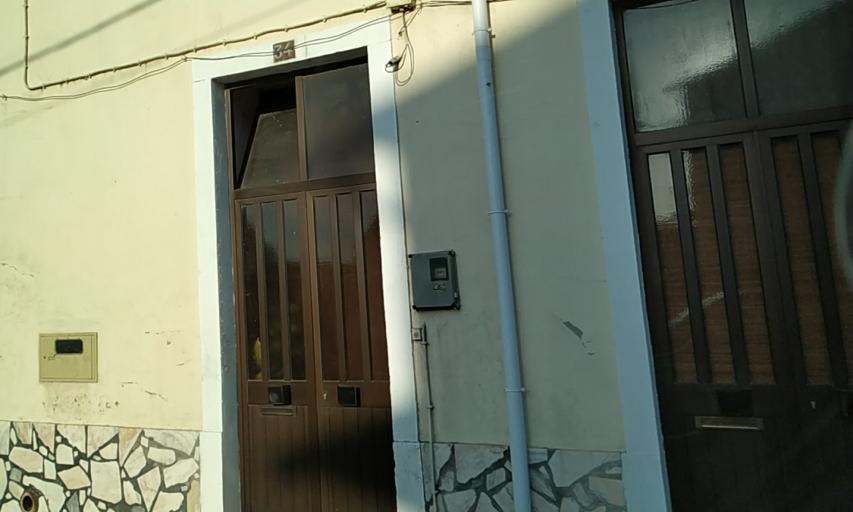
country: PT
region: Santarem
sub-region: Alcanena
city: Alcanena
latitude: 39.3801
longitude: -8.6608
